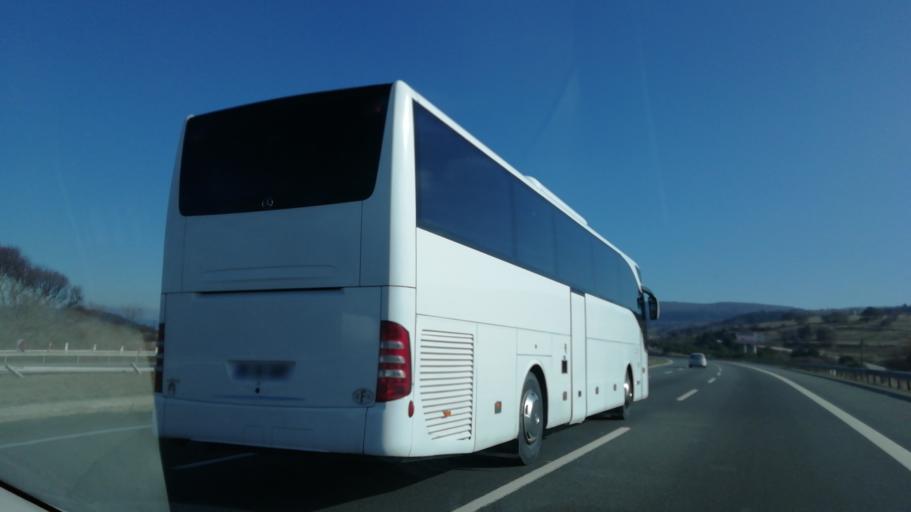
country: TR
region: Bolu
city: Yenicaga
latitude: 40.7509
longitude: 31.9314
